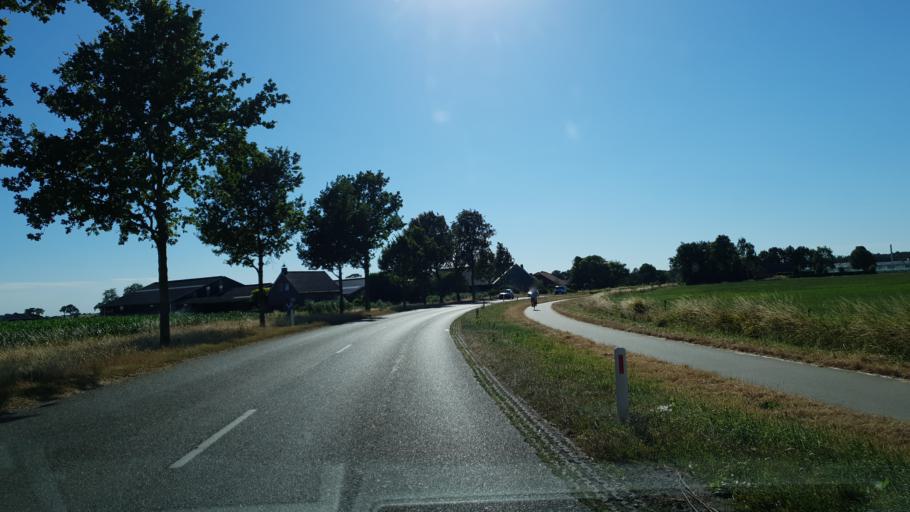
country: NL
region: North Brabant
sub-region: Gemeente Zundert
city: Zundert
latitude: 51.4757
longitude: 4.6330
